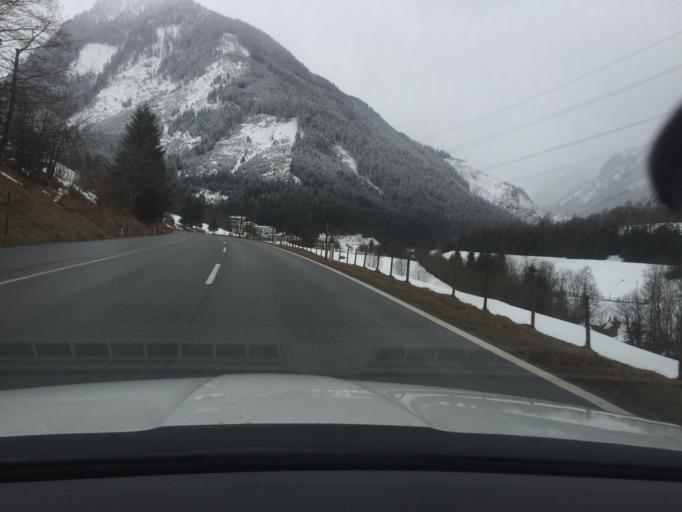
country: AT
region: Salzburg
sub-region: Politischer Bezirk Zell am See
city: Mittersill
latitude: 47.2303
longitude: 12.4926
